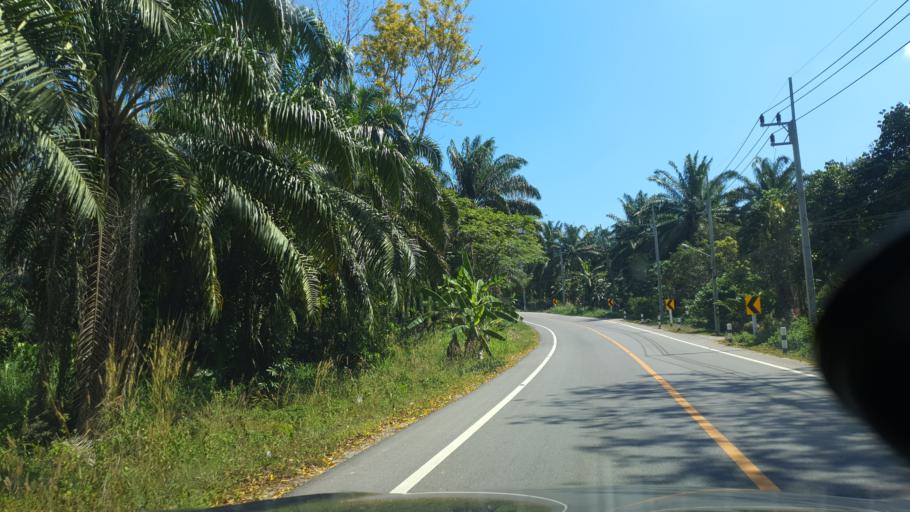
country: TH
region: Krabi
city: Khlong Thom
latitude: 7.9291
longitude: 99.2318
